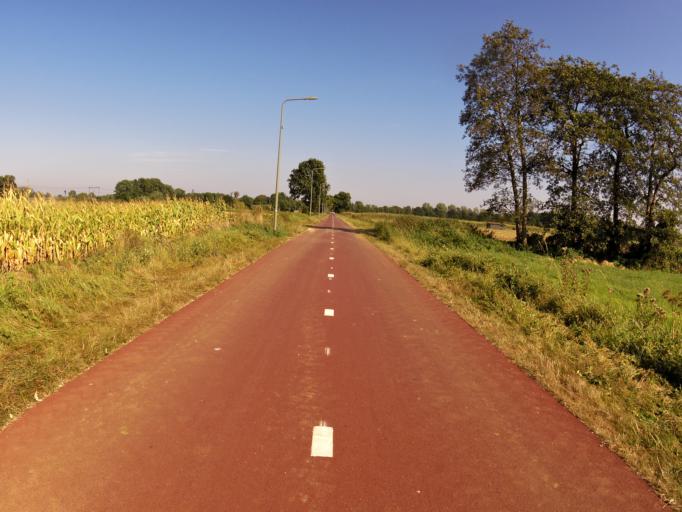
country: NL
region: North Brabant
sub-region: Gemeente Maasdonk
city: Geffen
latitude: 51.7493
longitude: 5.4818
